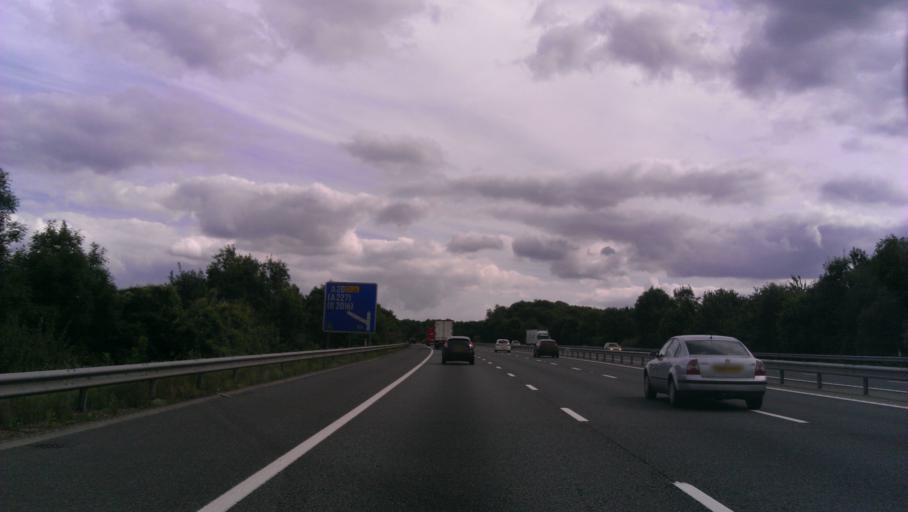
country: GB
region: England
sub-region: Kent
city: Borough Green
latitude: 51.3309
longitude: 0.2735
